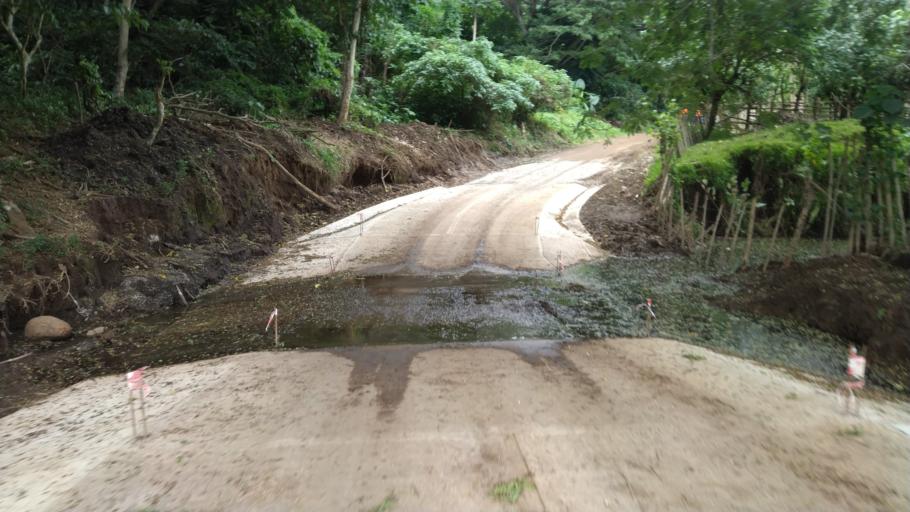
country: VU
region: Malampa
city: Lakatoro
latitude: -16.6128
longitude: 168.1625
